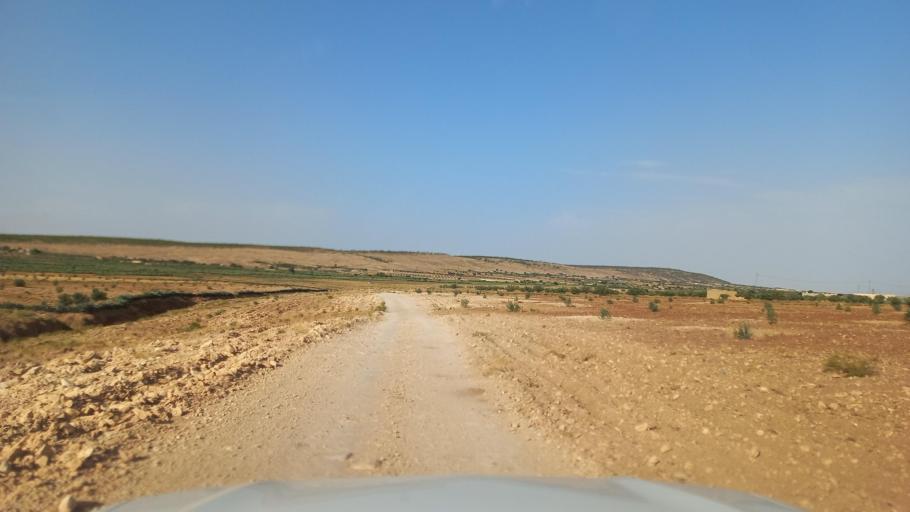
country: TN
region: Al Qasrayn
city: Kasserine
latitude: 35.3537
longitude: 8.8490
